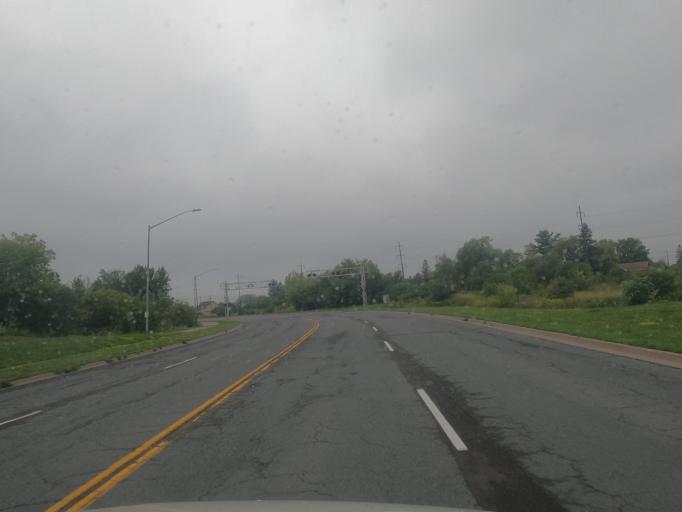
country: CA
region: Ontario
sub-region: Algoma
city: Sault Ste. Marie
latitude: 46.5342
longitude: -84.3456
